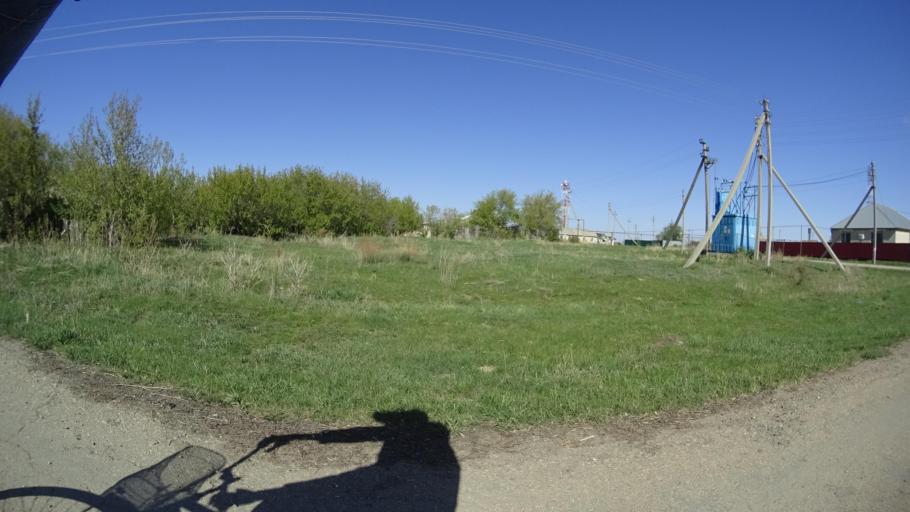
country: RU
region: Chelyabinsk
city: Chesma
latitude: 53.7919
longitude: 61.0359
